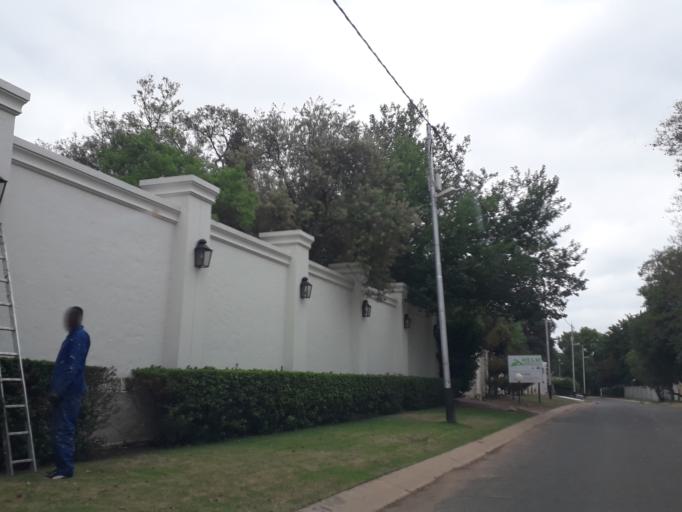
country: ZA
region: Gauteng
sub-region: City of Johannesburg Metropolitan Municipality
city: Midrand
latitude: -26.0438
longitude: 28.0374
